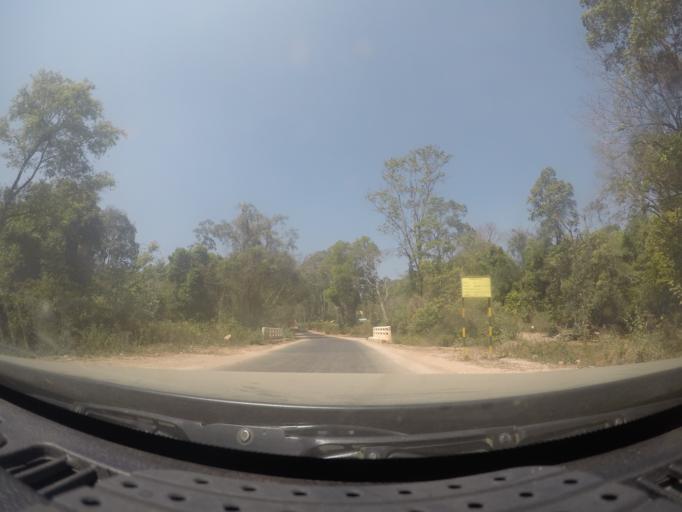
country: MM
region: Shan
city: Taunggyi
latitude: 20.9187
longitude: 96.5621
